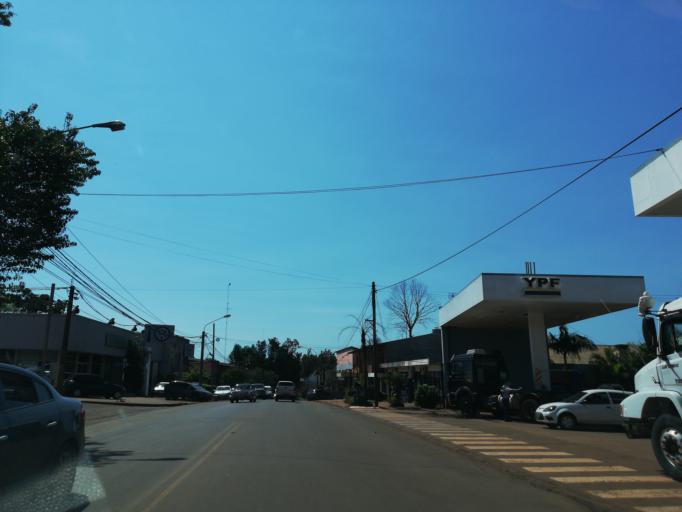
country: AR
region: Misiones
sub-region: Departamento de Eldorado
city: Eldorado
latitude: -26.4045
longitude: -54.6201
